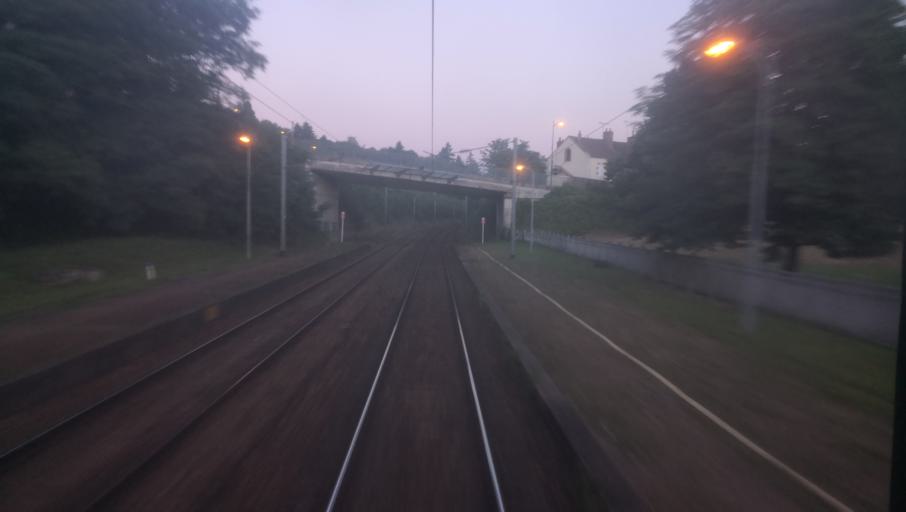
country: FR
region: Centre
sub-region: Departement du Loiret
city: Briare
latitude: 47.6462
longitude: 2.7342
